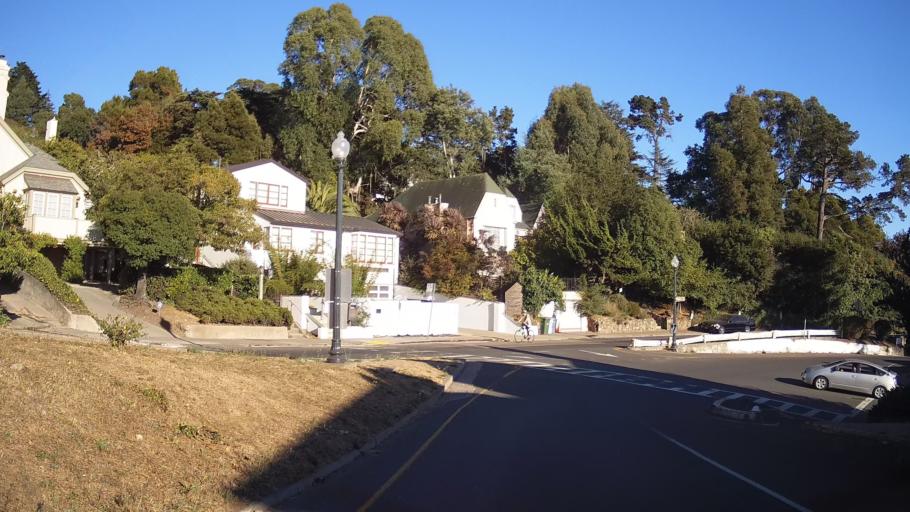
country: US
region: California
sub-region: Contra Costa County
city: Kensington
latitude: 37.8990
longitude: -122.2770
